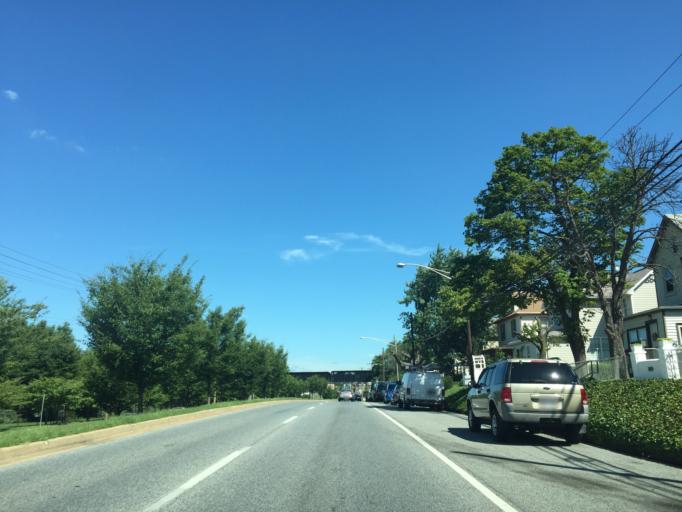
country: US
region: Maryland
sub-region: Baltimore County
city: Dundalk
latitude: 39.2683
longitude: -76.5289
